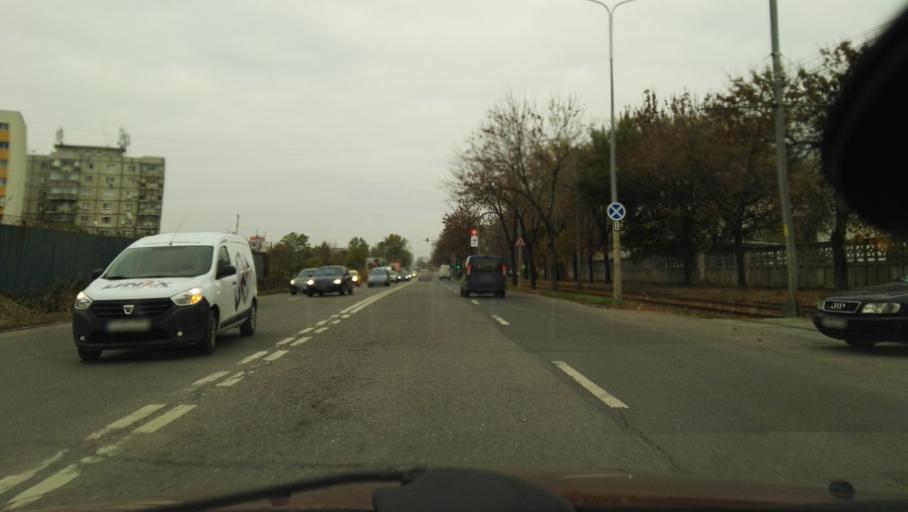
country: RO
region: Bucuresti
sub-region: Municipiul Bucuresti
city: Bucuresti
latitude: 44.4127
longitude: 26.0818
